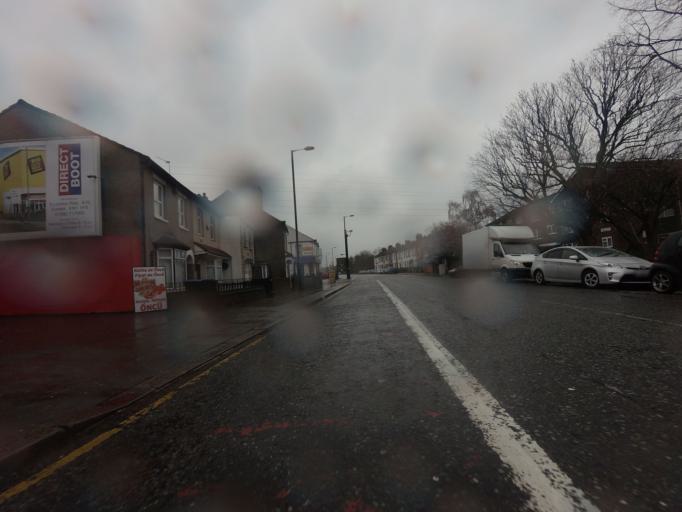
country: GB
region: England
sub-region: Hertfordshire
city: Waltham Cross
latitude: 51.6781
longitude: -0.0344
